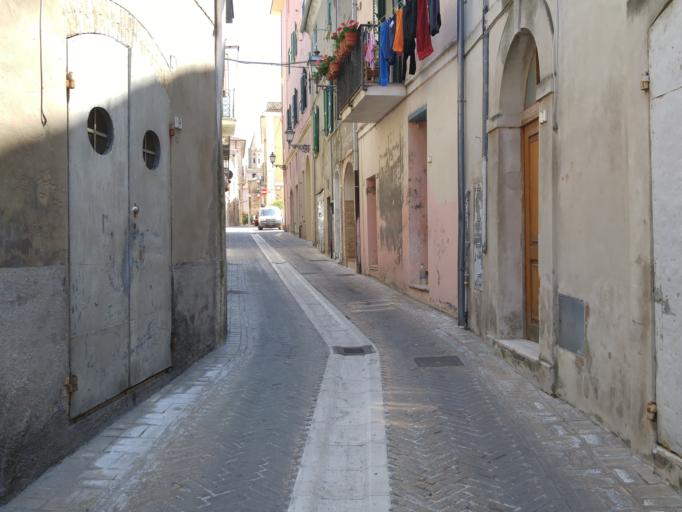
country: IT
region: Abruzzo
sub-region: Provincia di Pescara
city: Citta Sant'Angelo
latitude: 42.5180
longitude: 14.0576
